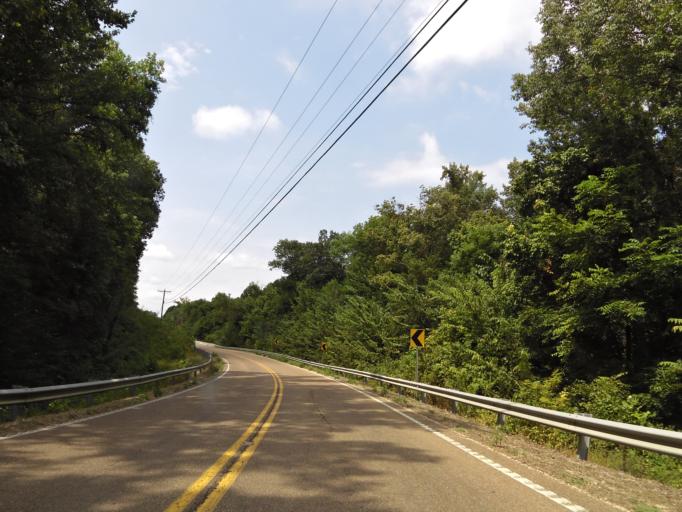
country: US
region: Tennessee
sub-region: Decatur County
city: Decaturville
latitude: 35.5804
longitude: -88.0913
